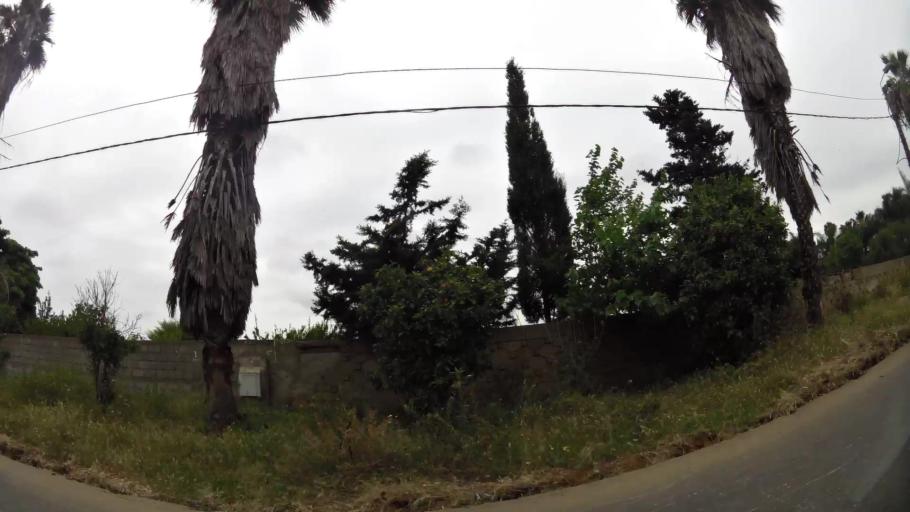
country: MA
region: Rabat-Sale-Zemmour-Zaer
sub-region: Rabat
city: Rabat
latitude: 33.9646
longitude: -6.8145
